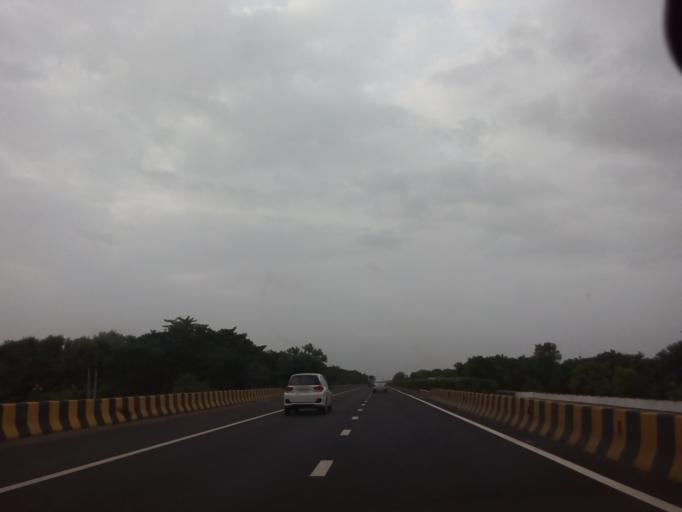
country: IN
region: Gujarat
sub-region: Kheda
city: Nadiad
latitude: 22.6874
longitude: 72.9045
